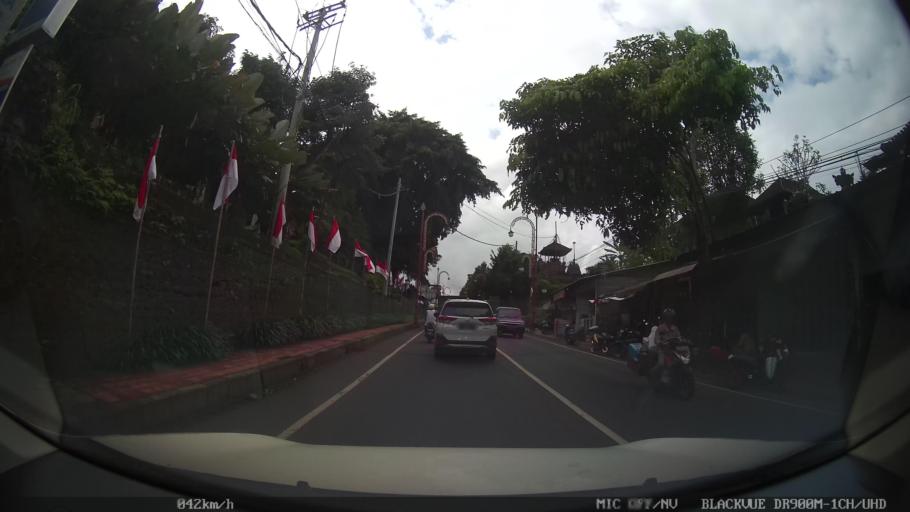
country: ID
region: Bali
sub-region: Kabupaten Gianyar
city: Ubud
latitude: -8.5347
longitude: 115.3116
